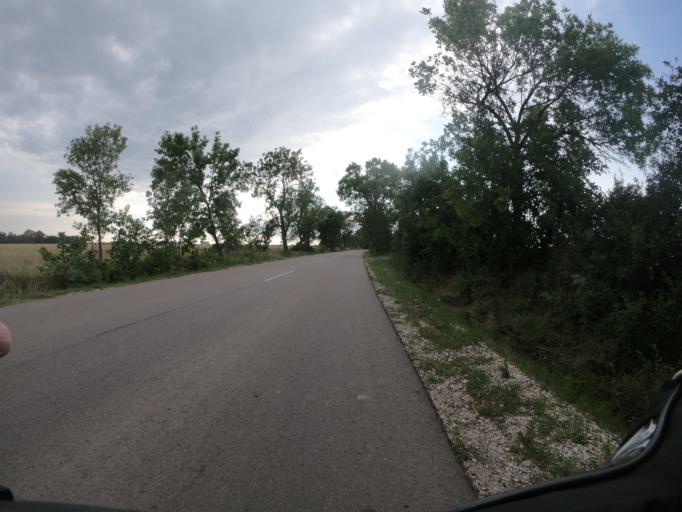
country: HU
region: Borsod-Abauj-Zemplen
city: Mezocsat
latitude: 47.8177
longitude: 20.8721
